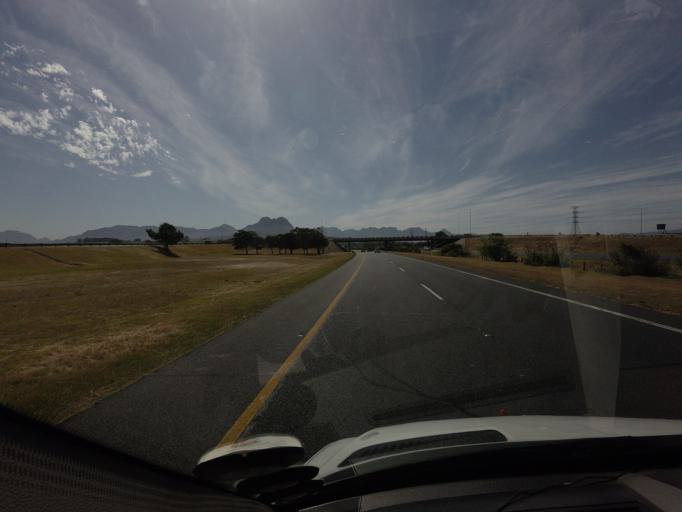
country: ZA
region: Western Cape
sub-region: Cape Winelands District Municipality
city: Stellenbosch
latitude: -34.0594
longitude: 18.7794
